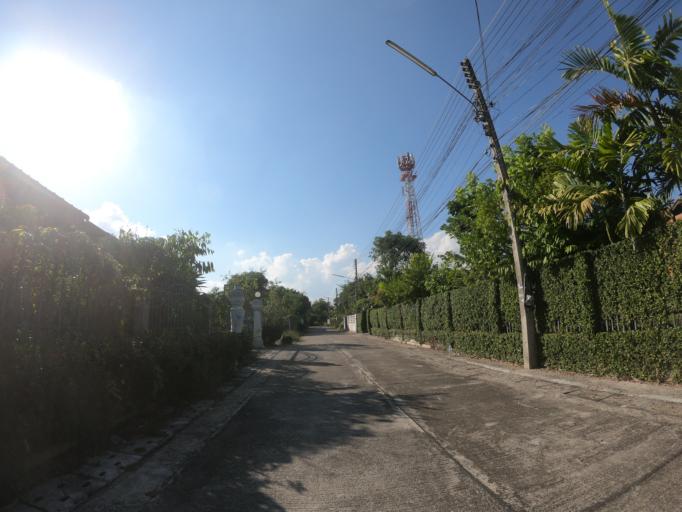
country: TH
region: Chiang Mai
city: Chiang Mai
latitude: 18.7546
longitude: 98.9725
